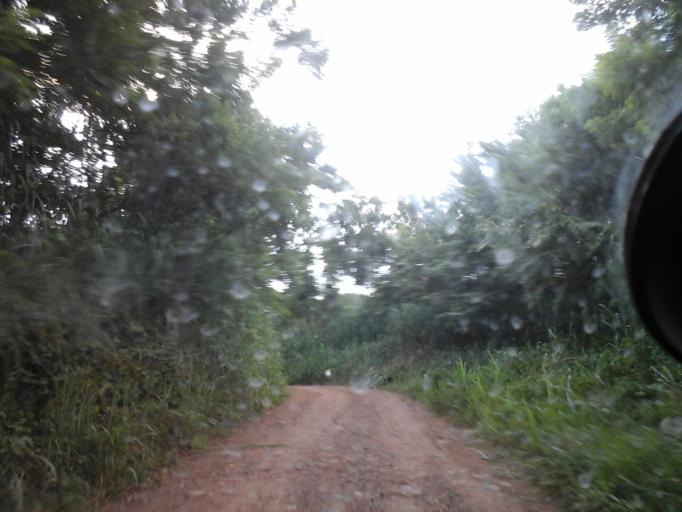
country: CO
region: Cesar
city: San Diego
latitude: 10.2506
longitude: -73.1150
